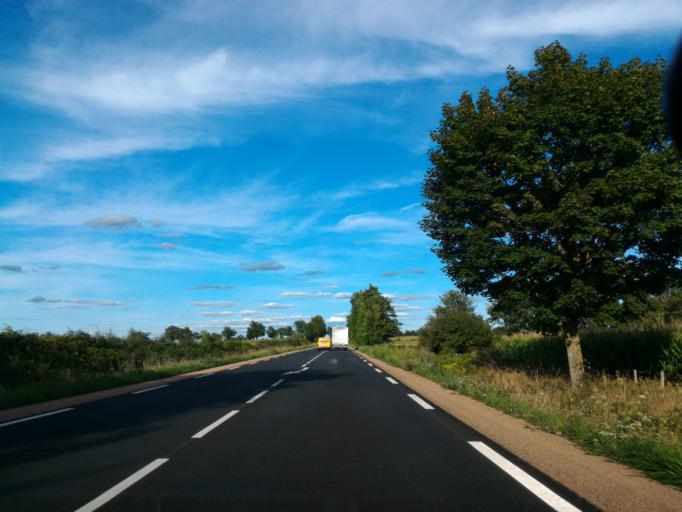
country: FR
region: Limousin
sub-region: Departement de la Haute-Vienne
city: Chateauponsac
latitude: 46.1948
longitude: 1.2688
